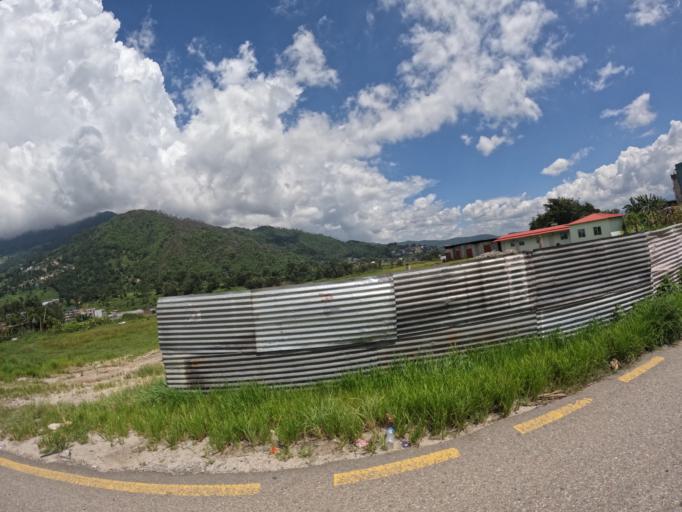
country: NP
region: Central Region
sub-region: Bagmati Zone
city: Kathmandu
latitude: 27.7803
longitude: 85.3251
